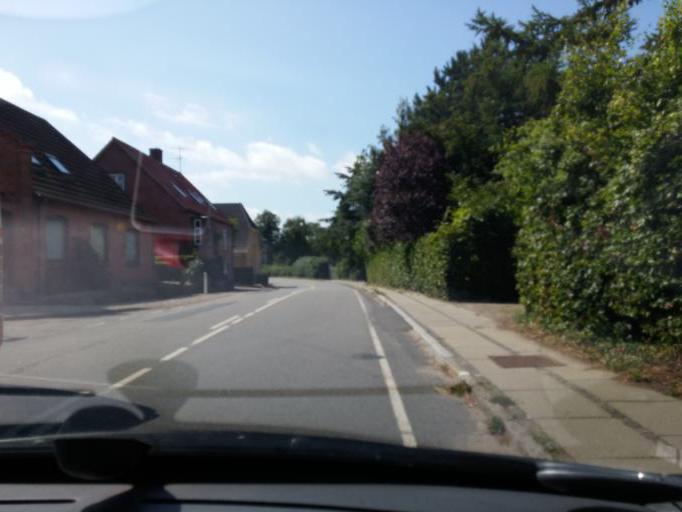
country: DK
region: South Denmark
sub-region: Langeland Kommune
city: Rudkobing
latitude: 54.8260
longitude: 10.6940
